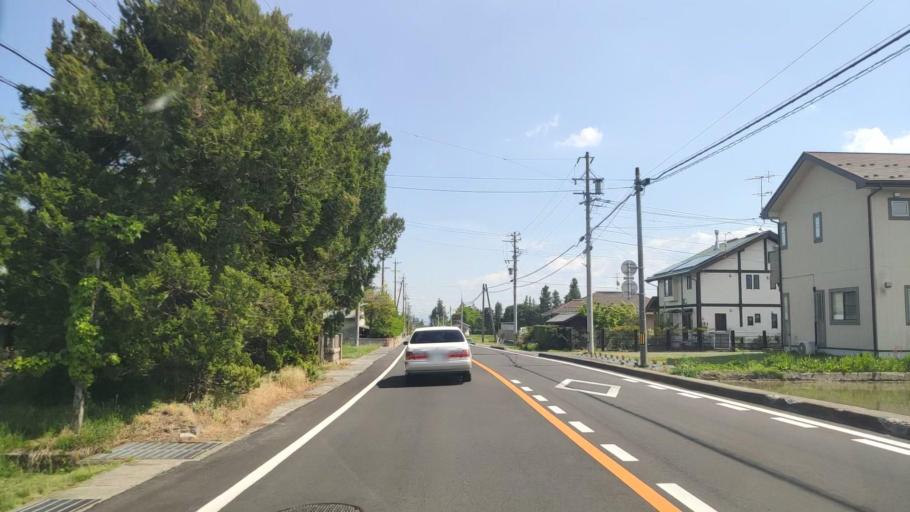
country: JP
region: Nagano
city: Hotaka
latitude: 36.4003
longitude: 137.8615
